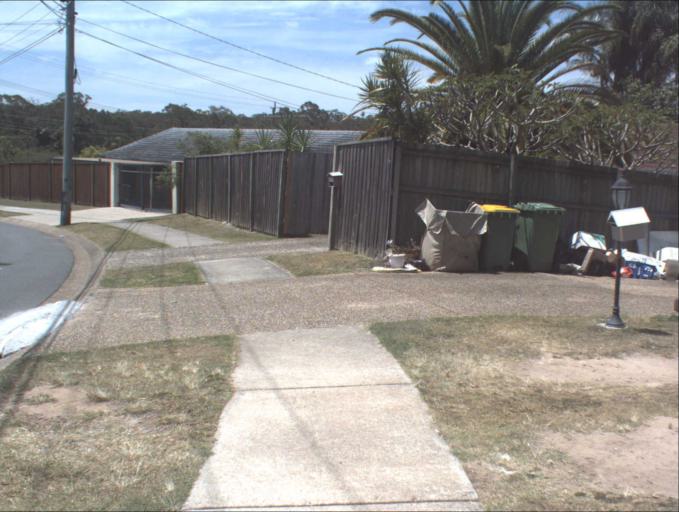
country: AU
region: Queensland
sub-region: Logan
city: Rochedale South
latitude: -27.5965
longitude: 153.1439
